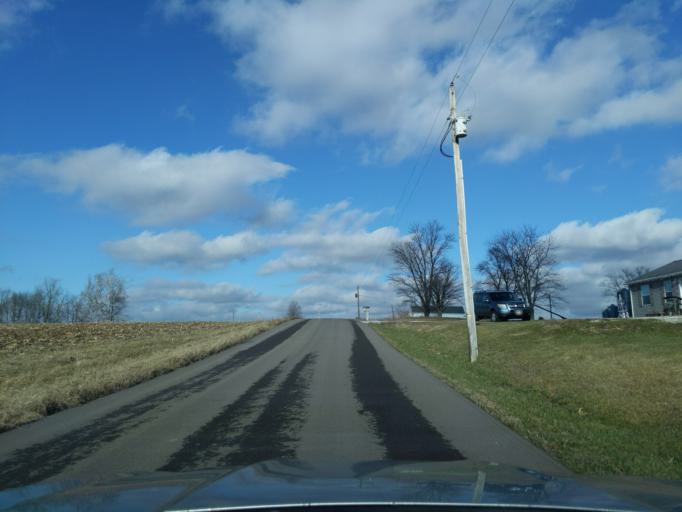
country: US
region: Indiana
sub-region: Decatur County
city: Greensburg
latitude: 39.2668
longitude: -85.4839
